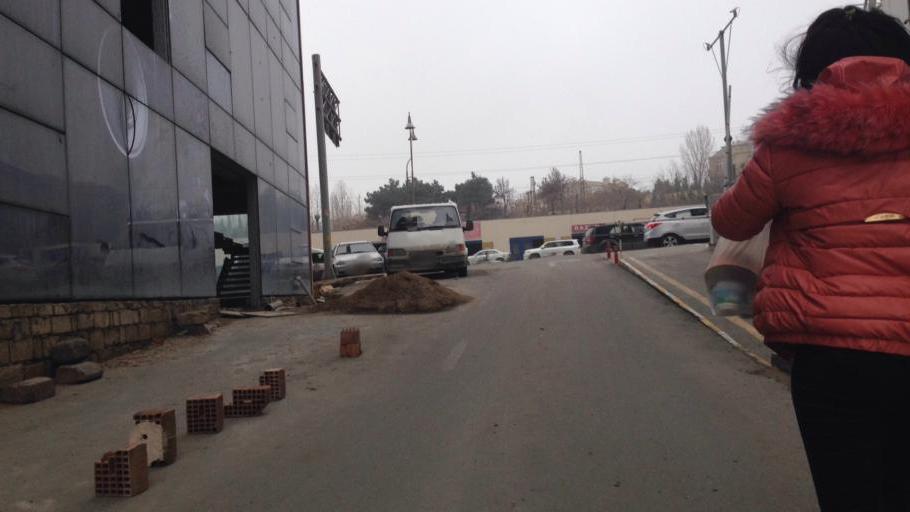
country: AZ
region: Baki
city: Baku
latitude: 40.3884
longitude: 49.8719
